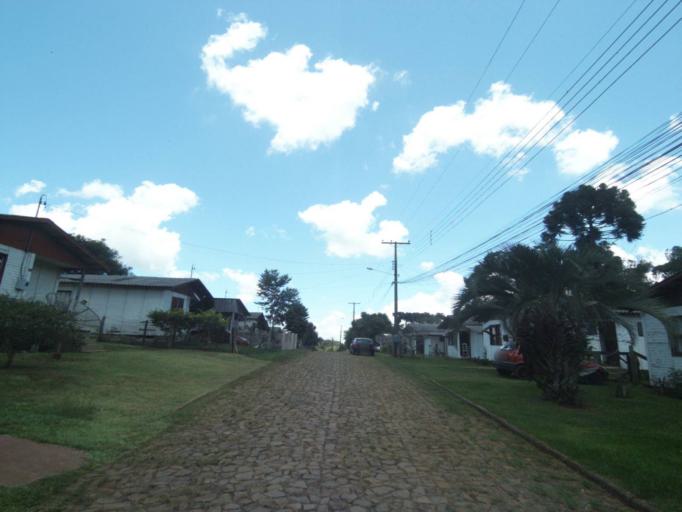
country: BR
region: Parana
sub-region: Pinhao
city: Pinhao
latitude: -25.7879
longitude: -52.0852
